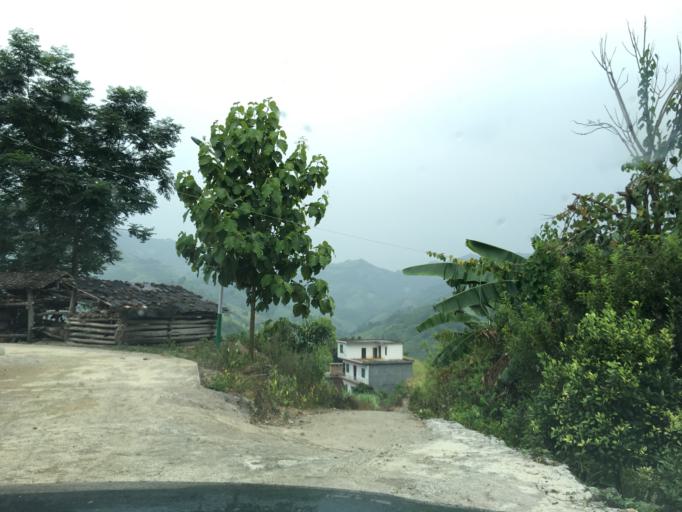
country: CN
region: Guangxi Zhuangzu Zizhiqu
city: Tongle
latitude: 25.0001
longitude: 105.9941
